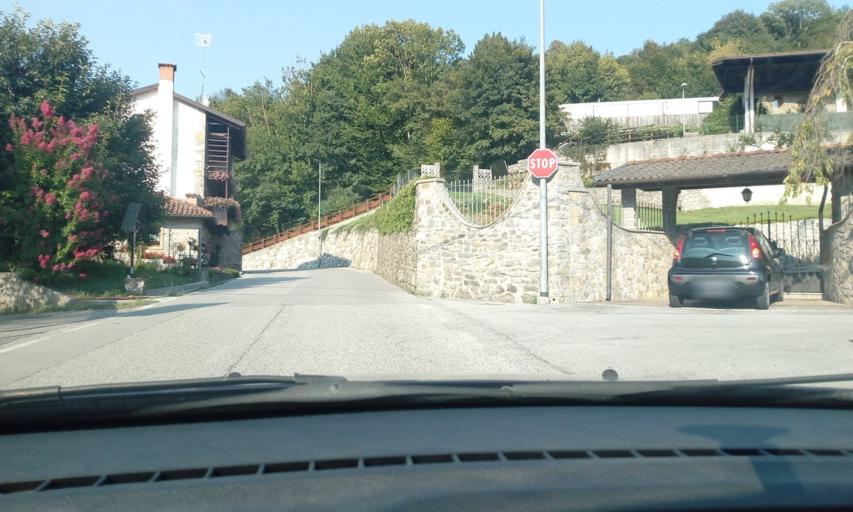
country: IT
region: Friuli Venezia Giulia
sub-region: Provincia di Udine
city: Merso di Sopra
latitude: 46.1338
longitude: 13.5361
